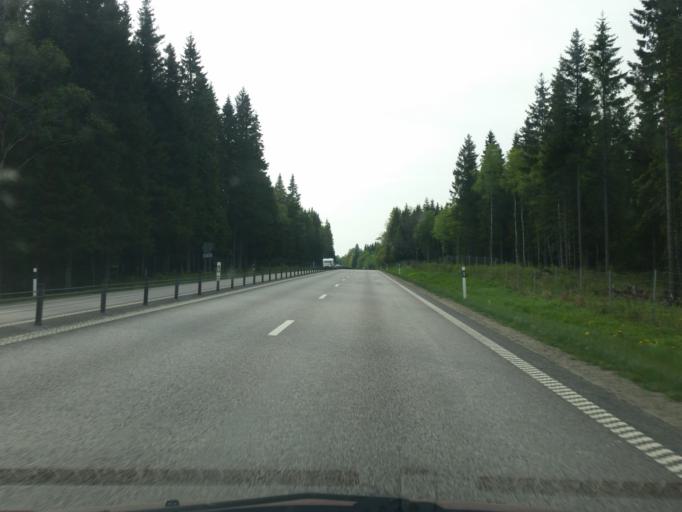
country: SE
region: Vaestra Goetaland
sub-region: Ulricehamns Kommun
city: Ulricehamn
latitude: 57.7983
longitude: 13.5315
